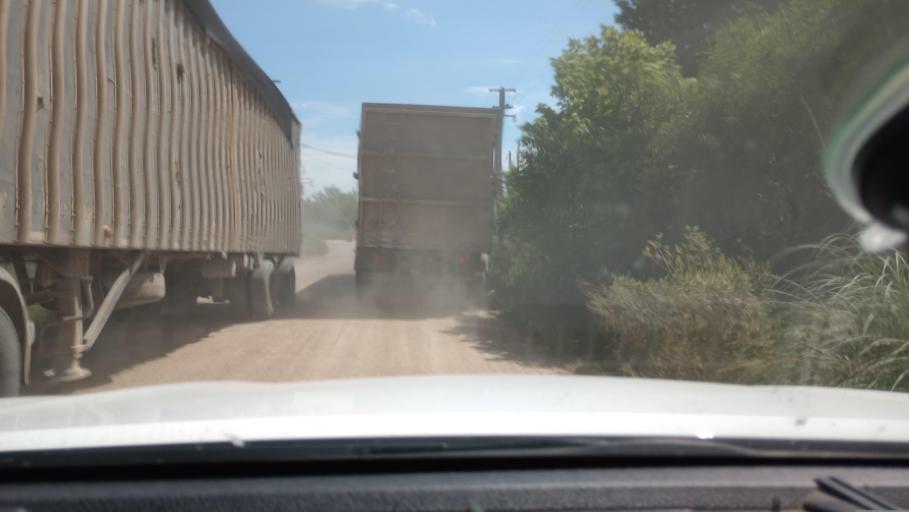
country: UY
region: Canelones
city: Sauce
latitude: -34.6604
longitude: -56.0594
